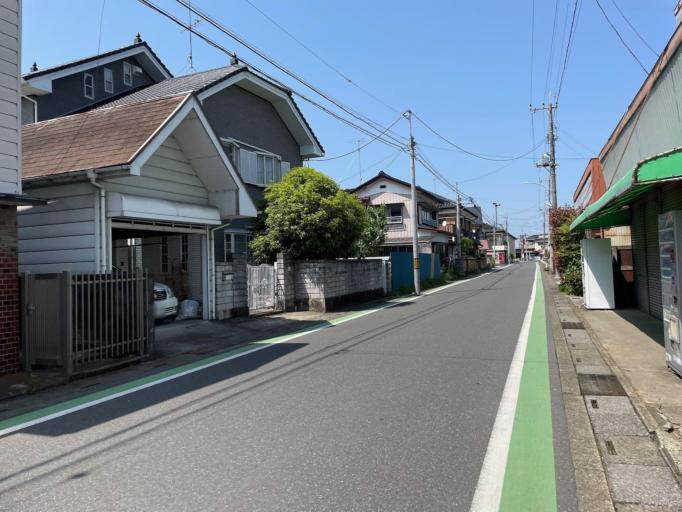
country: JP
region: Tochigi
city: Fujioka
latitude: 36.2047
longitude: 139.6581
